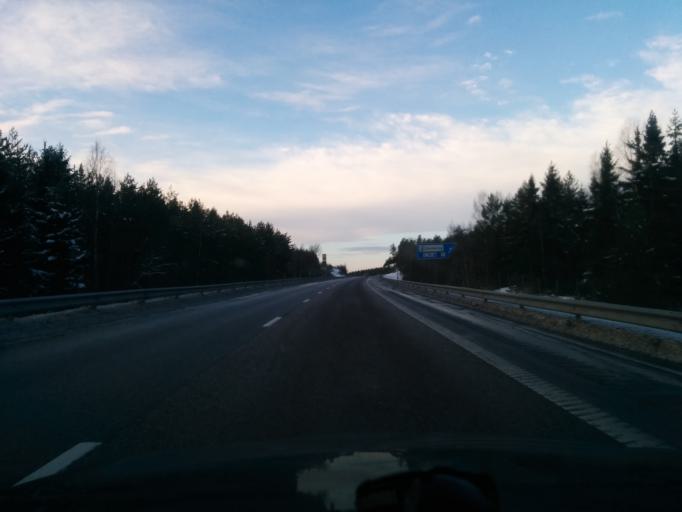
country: SE
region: Uppsala
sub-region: Enkopings Kommun
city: Dalby
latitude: 59.6159
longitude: 17.4052
